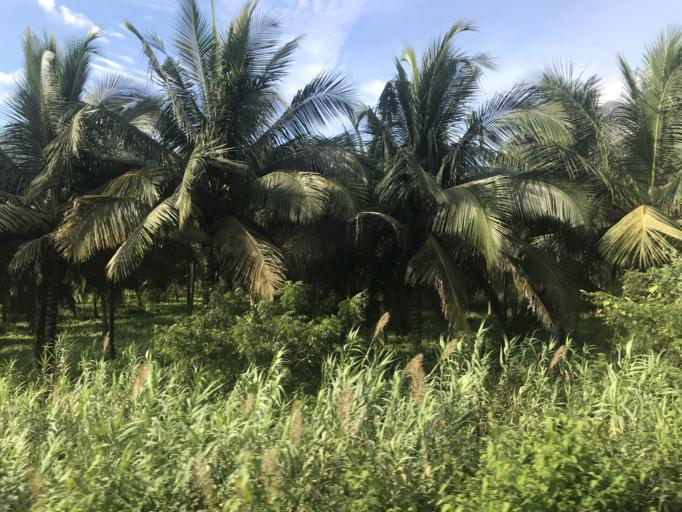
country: IN
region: Tamil Nadu
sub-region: Coimbatore
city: Madukkarai
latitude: 10.8837
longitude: 76.8721
